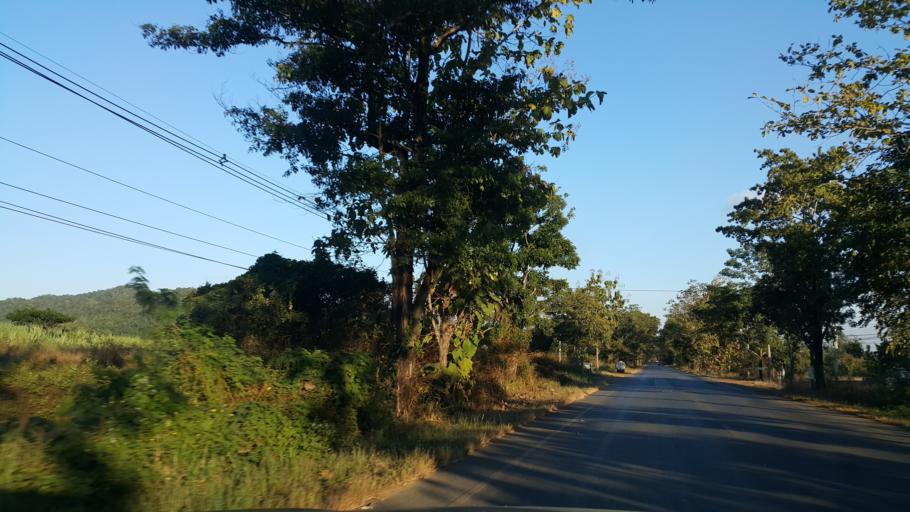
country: TH
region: Sukhothai
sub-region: Amphoe Si Satchanalai
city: Si Satchanalai
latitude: 17.5506
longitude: 99.8865
